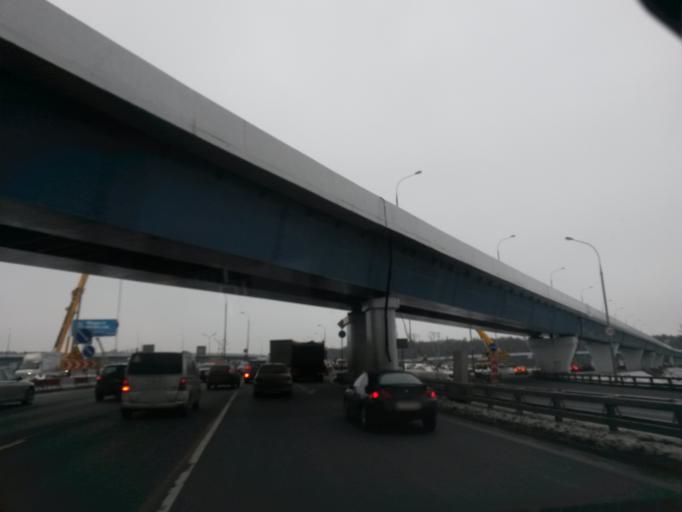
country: RU
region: Moskovskaya
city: Mosrentgen
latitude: 55.6410
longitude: 37.4568
